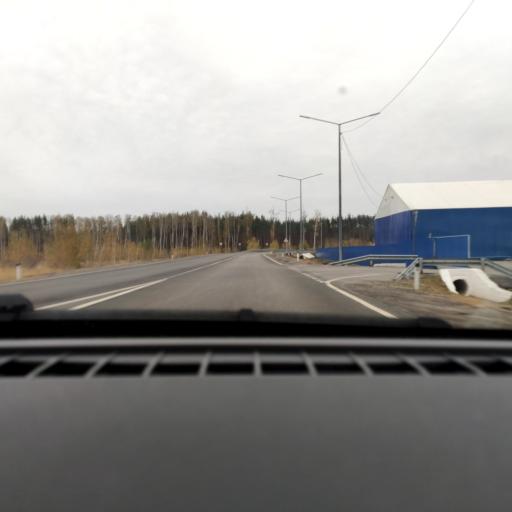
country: RU
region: Voronezj
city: Somovo
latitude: 51.7434
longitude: 39.3087
